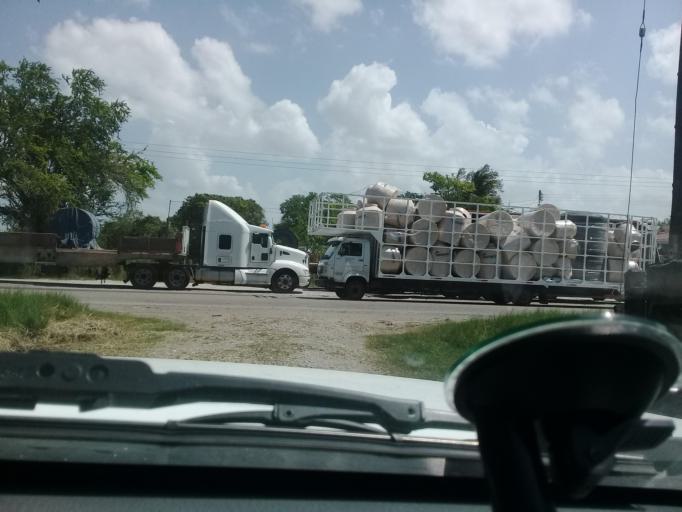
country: MX
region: Veracruz
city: Moralillo
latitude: 22.1718
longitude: -98.0493
